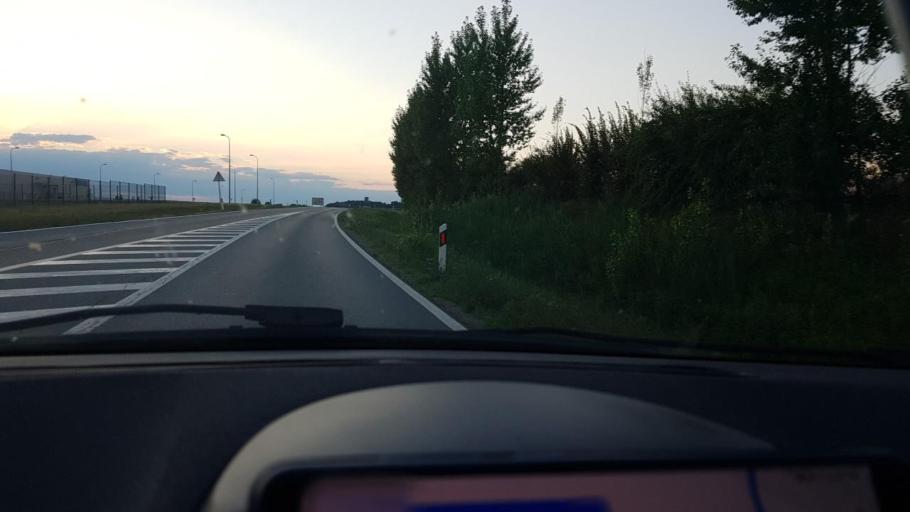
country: HR
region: Bjelovarsko-Bilogorska
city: Zdralovi
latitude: 45.8432
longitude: 16.9485
